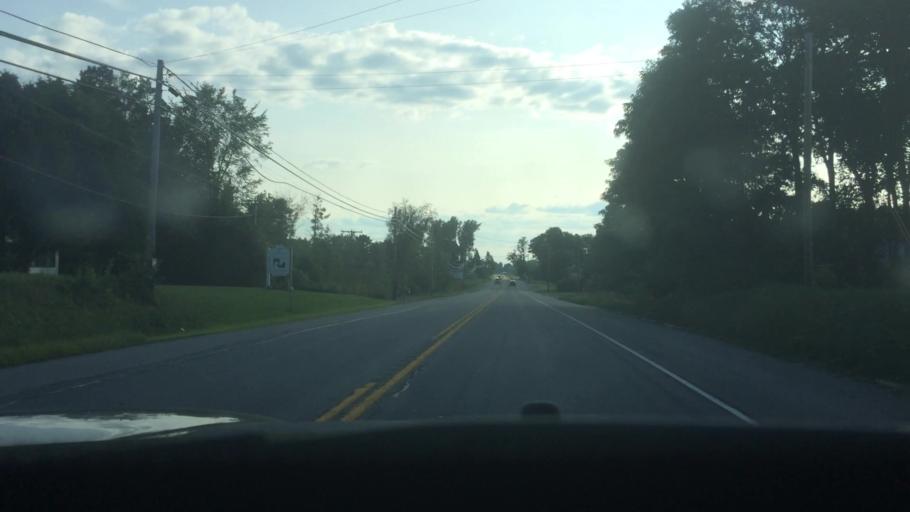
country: US
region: New York
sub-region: St. Lawrence County
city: Potsdam
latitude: 44.6382
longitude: -75.0714
